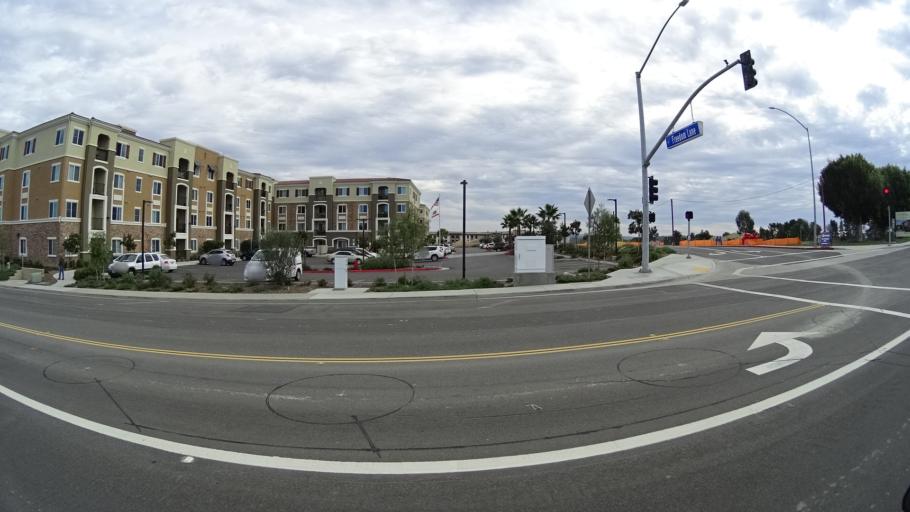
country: US
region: California
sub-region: Orange County
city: Aliso Viejo
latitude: 33.5629
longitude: -117.7305
